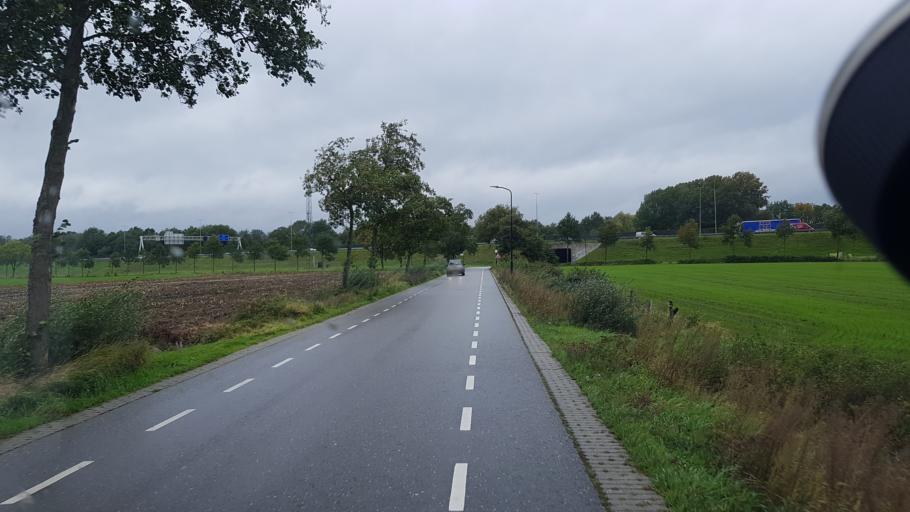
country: NL
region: Gelderland
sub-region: Gemeente Apeldoorn
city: Apeldoorn
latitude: 52.1820
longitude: 6.0083
